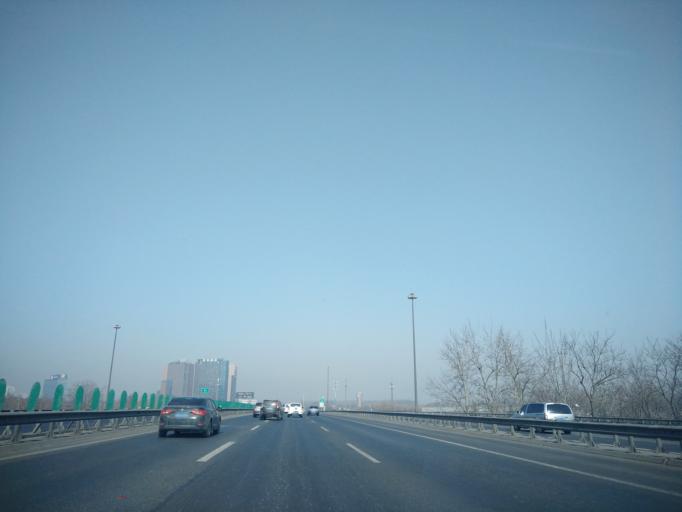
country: CN
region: Beijing
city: Wangjing
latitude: 39.9983
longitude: 116.4936
